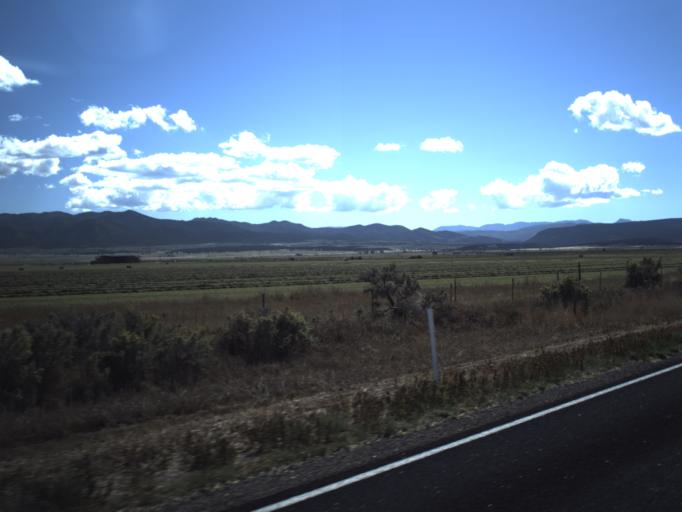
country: US
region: Utah
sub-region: Washington County
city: Enterprise
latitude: 37.6318
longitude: -113.6612
